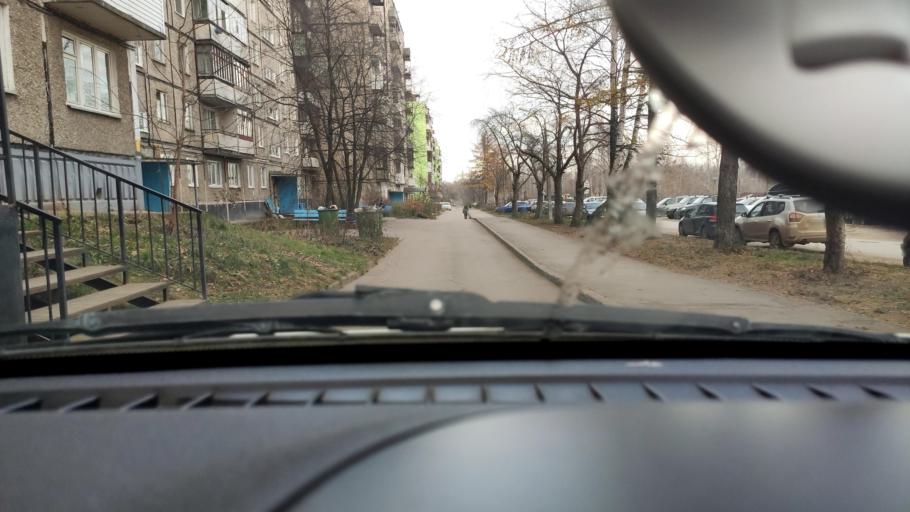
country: RU
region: Perm
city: Perm
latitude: 58.1110
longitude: 56.3810
